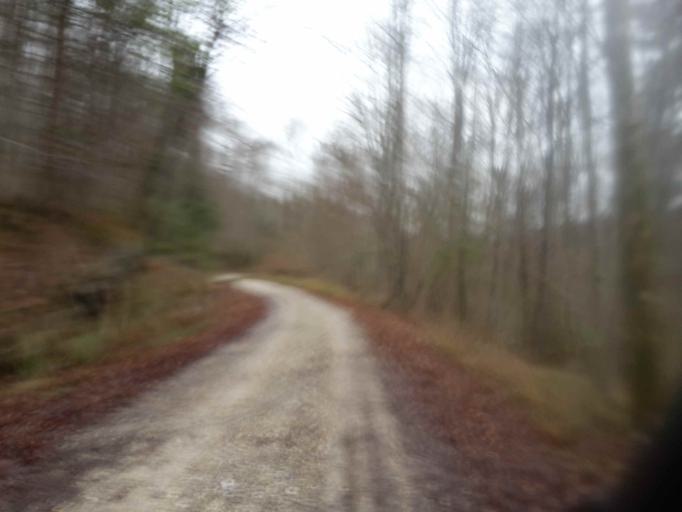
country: DE
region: Bavaria
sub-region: Upper Bavaria
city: Baierbrunn
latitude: 48.0098
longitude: 11.4804
